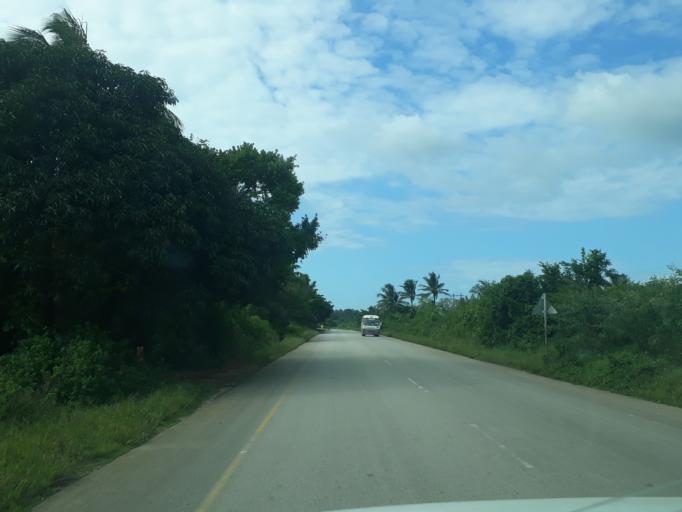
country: TZ
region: Zanzibar North
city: Kijini
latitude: -5.8393
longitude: 39.2855
